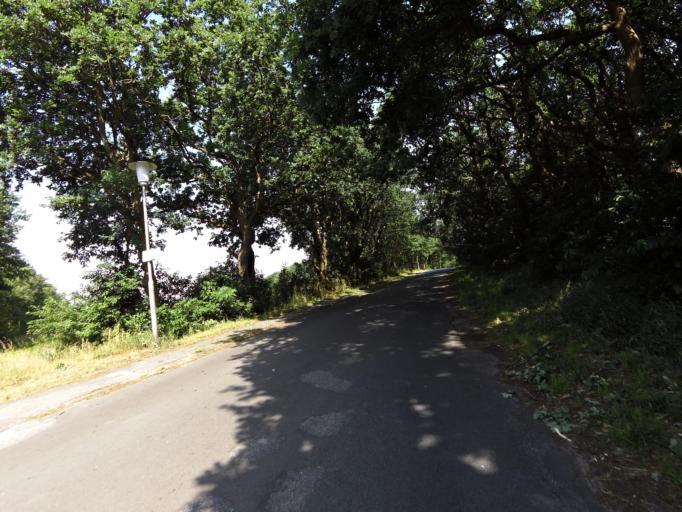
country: DE
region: Lower Saxony
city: Nordholz
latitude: 53.8240
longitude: 8.5874
